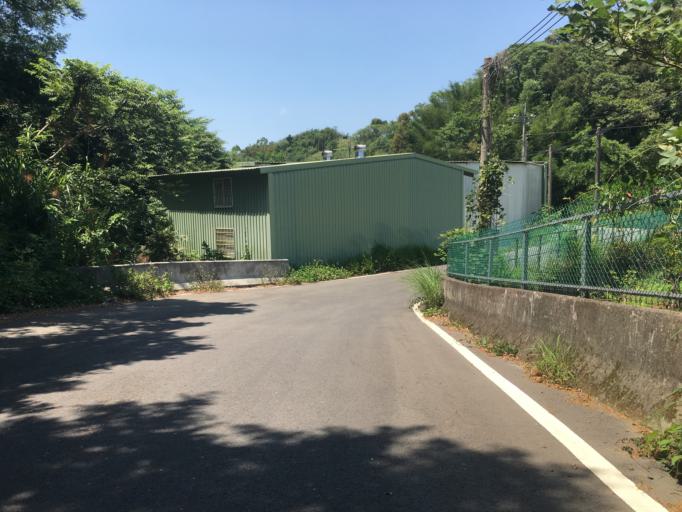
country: TW
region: Taiwan
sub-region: Hsinchu
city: Hsinchu
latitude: 24.7349
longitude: 120.9797
